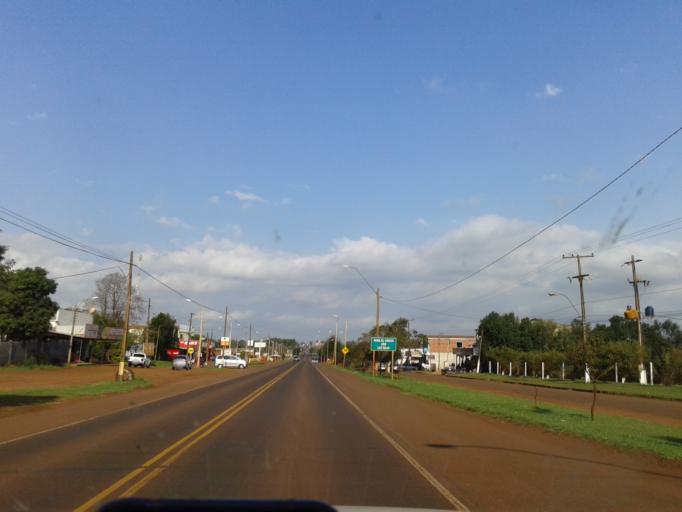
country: PY
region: Itapua
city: Arquitecto Tomas Romero Pereira
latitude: -26.5129
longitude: -55.2739
